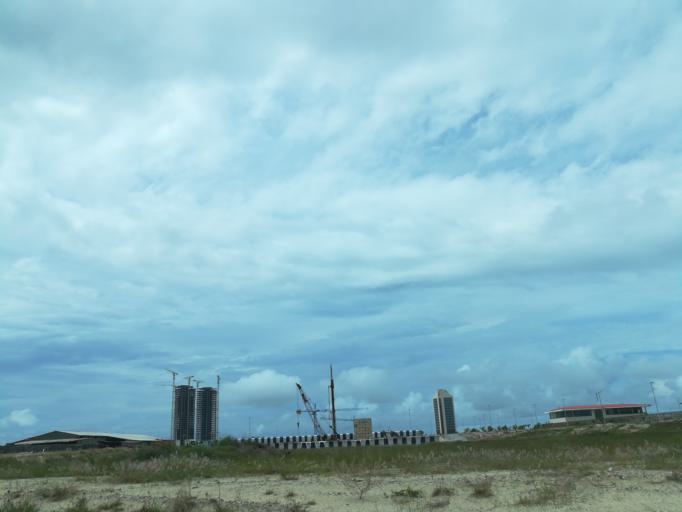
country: NG
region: Lagos
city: Lagos
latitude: 6.4141
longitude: 3.4083
